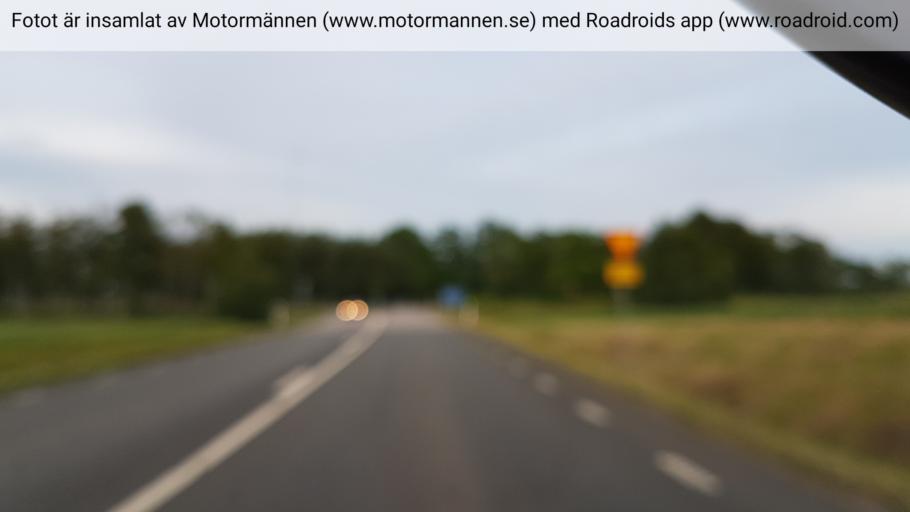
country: SE
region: Vaestra Goetaland
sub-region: Falkopings Kommun
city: Falkoeping
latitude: 58.1791
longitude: 13.5845
